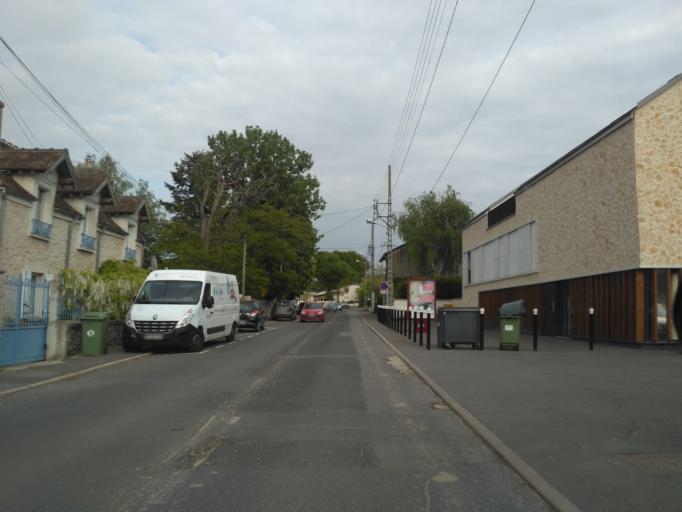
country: FR
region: Ile-de-France
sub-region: Departement de Seine-et-Marne
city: Cesson
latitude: 48.5627
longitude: 2.6074
